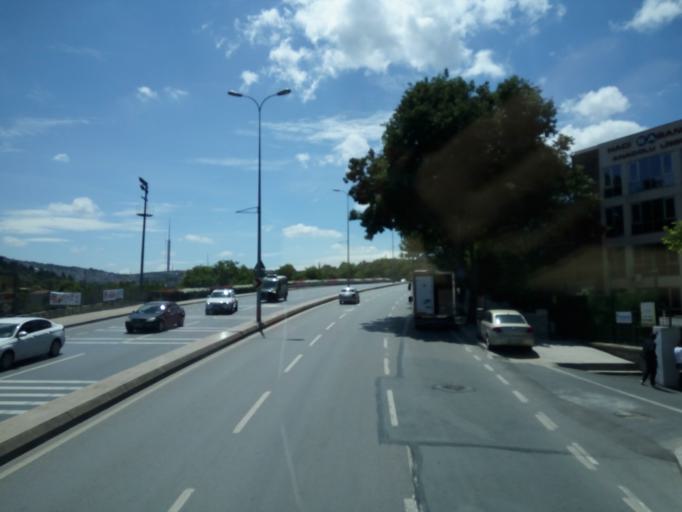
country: TR
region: Istanbul
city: UEskuedar
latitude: 41.0422
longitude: 29.0420
